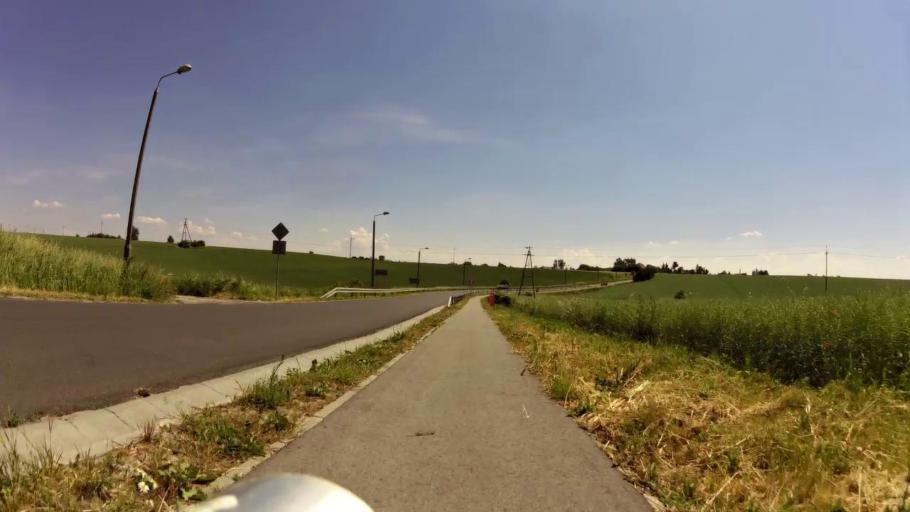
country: PL
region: Kujawsko-Pomorskie
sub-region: Powiat nakielski
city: Slesin
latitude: 53.1708
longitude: 17.7060
